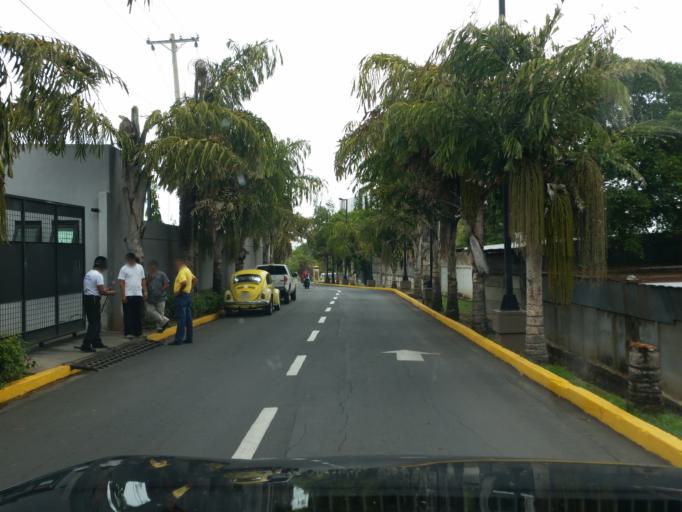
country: NI
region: Managua
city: Managua
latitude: 12.1287
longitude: -86.2639
